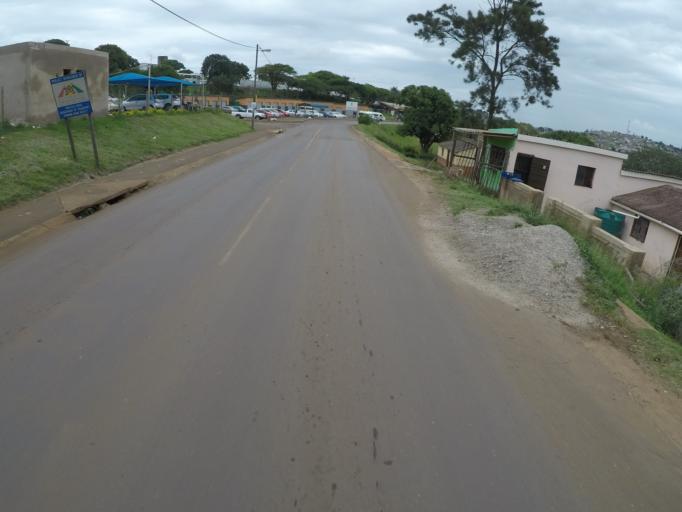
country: ZA
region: KwaZulu-Natal
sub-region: uThungulu District Municipality
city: Empangeni
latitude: -28.7762
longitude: 31.8650
